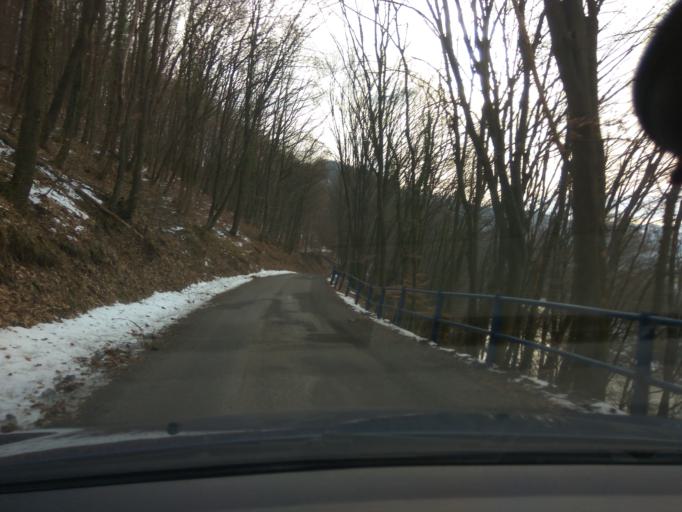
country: SK
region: Banskobystricky
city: Zarnovica
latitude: 48.4815
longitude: 18.7347
